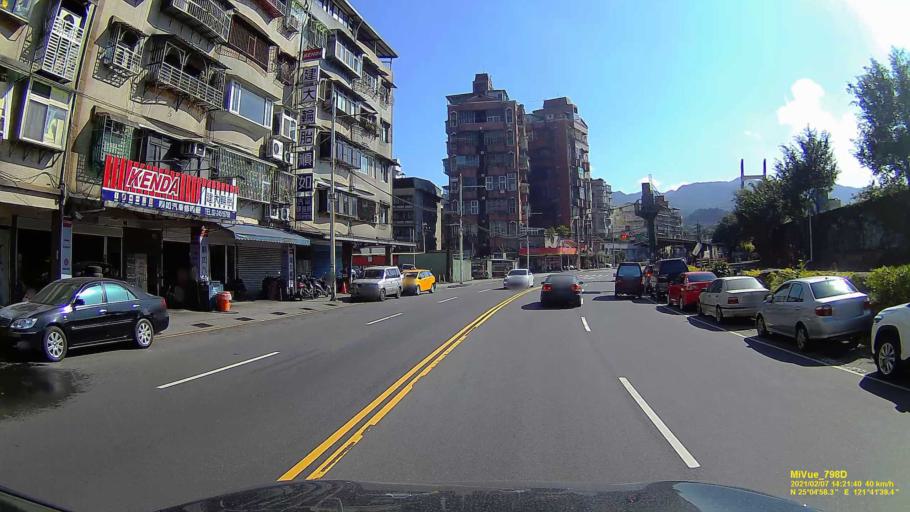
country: TW
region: Taiwan
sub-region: Keelung
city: Keelung
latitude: 25.0826
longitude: 121.6943
